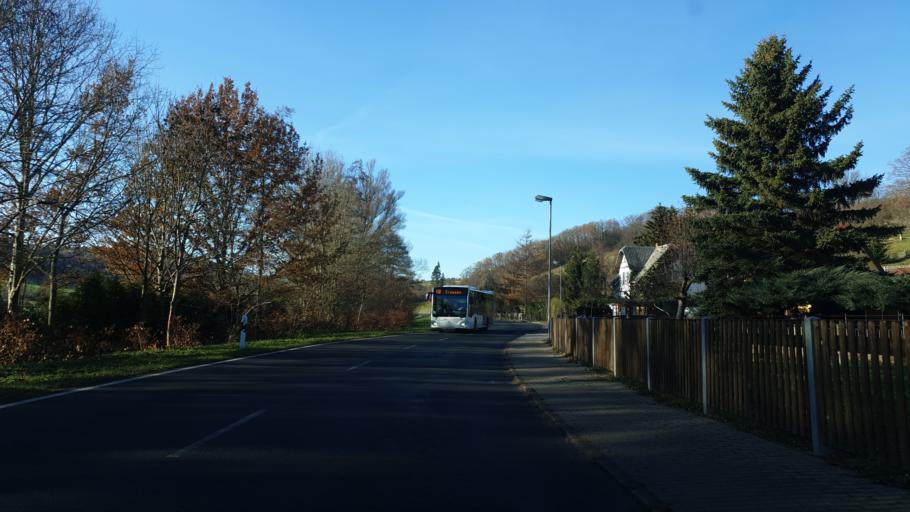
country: DE
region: Thuringia
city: Rauda
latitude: 50.9523
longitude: 11.9389
